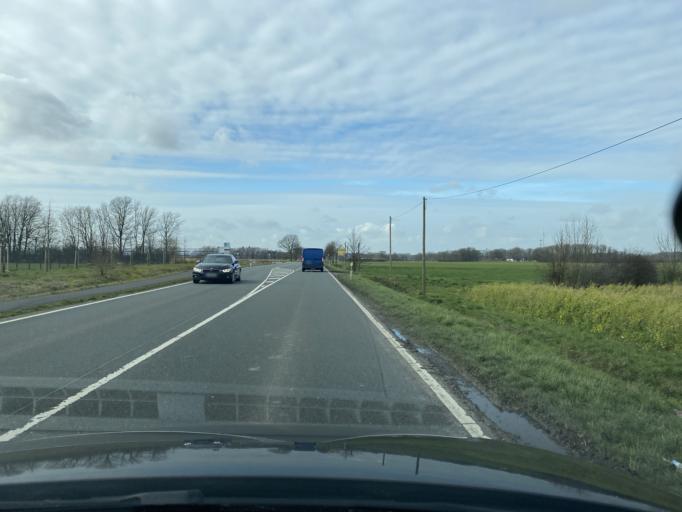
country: DE
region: North Rhine-Westphalia
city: Oelde
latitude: 51.8338
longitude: 8.2152
